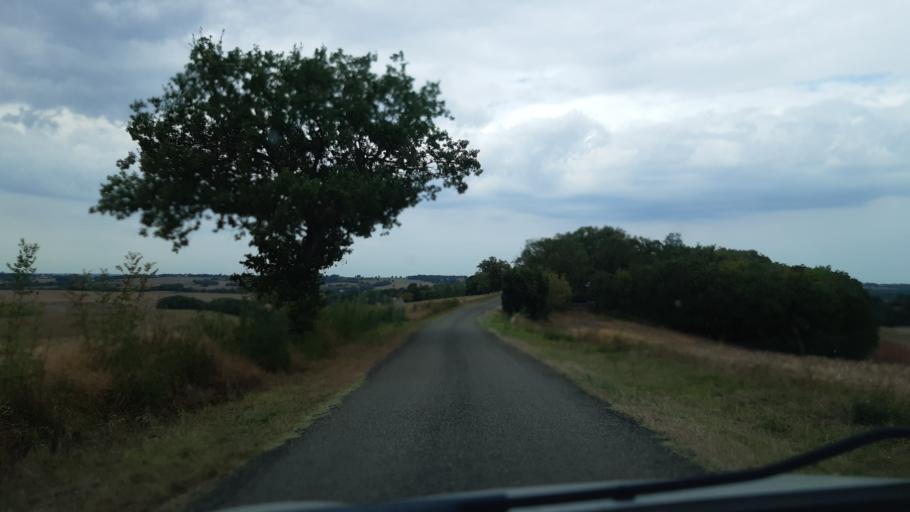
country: FR
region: Midi-Pyrenees
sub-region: Departement du Gers
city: Gimont
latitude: 43.7003
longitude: 0.9946
